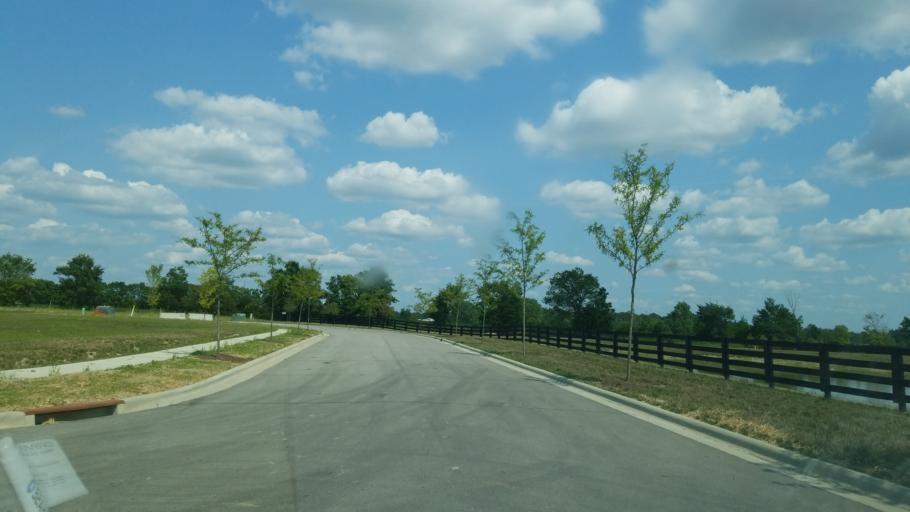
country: US
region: Ohio
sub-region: Union County
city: New California
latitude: 40.1886
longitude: -83.1727
